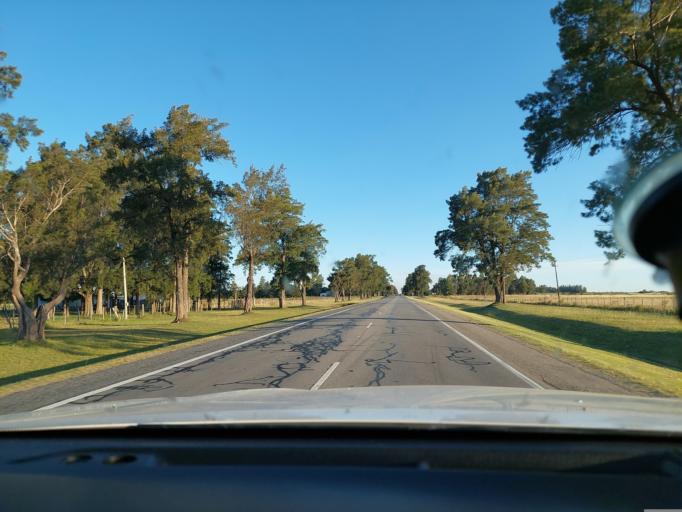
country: UY
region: Canelones
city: San Jacinto
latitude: -34.5747
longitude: -55.8492
